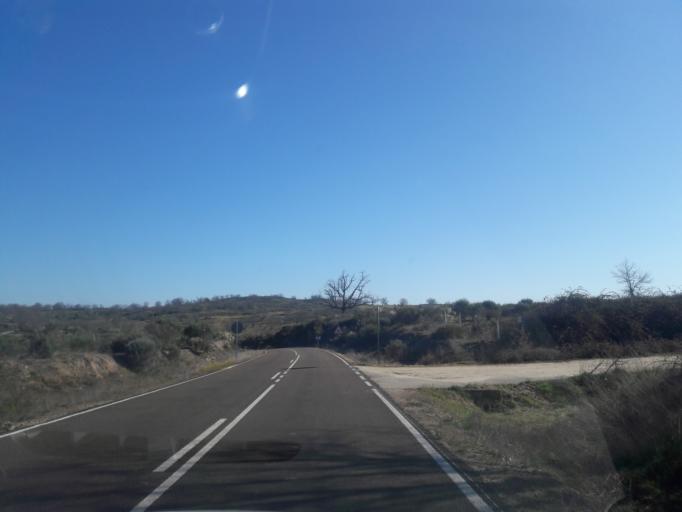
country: ES
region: Castille and Leon
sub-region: Provincia de Salamanca
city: Cabeza del Caballo
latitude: 41.0961
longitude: -6.5532
